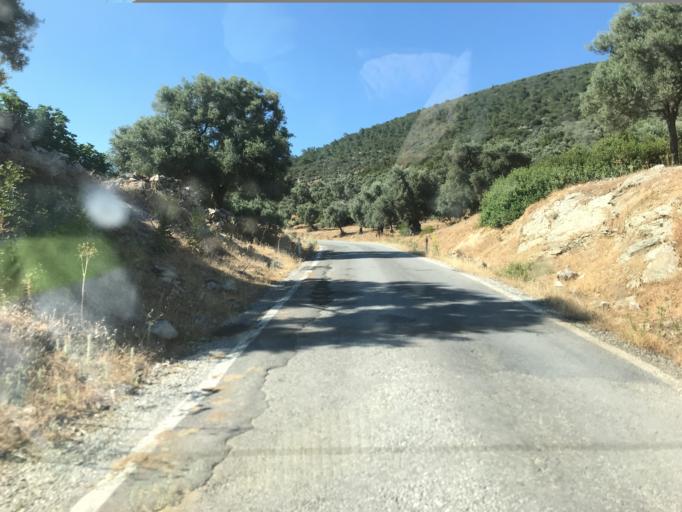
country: TR
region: Mugla
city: Selimiye
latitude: 37.3746
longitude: 27.4906
